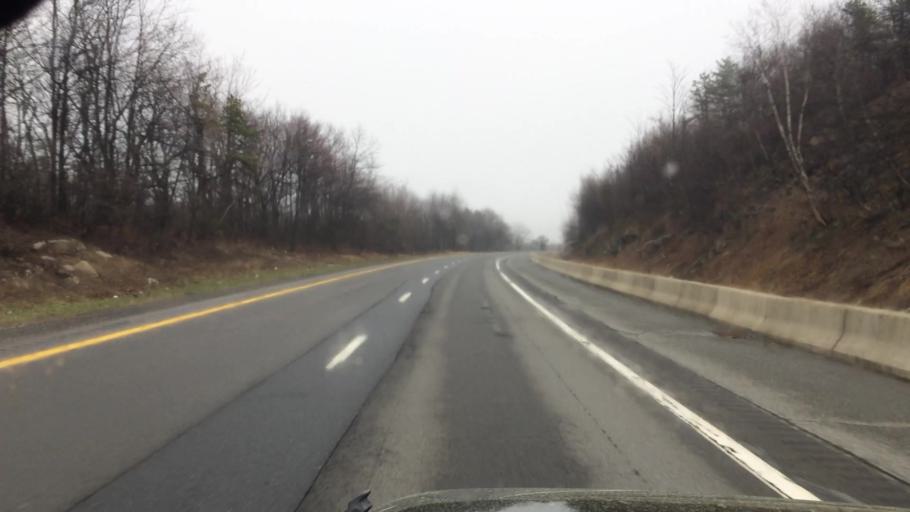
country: US
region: Pennsylvania
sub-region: Schuylkill County
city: Frackville
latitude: 40.7701
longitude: -76.2584
